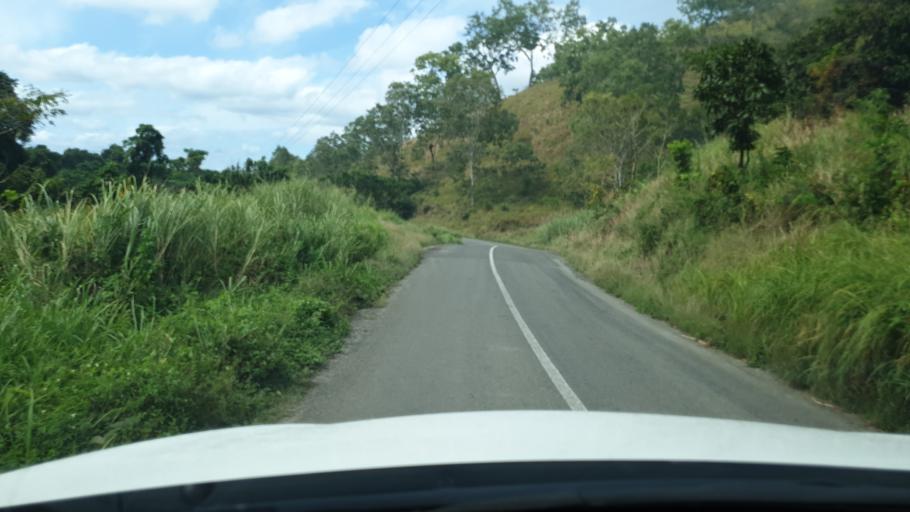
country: PG
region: Central Province
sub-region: Rigo
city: Kwikila
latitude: -9.8300
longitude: 147.5637
